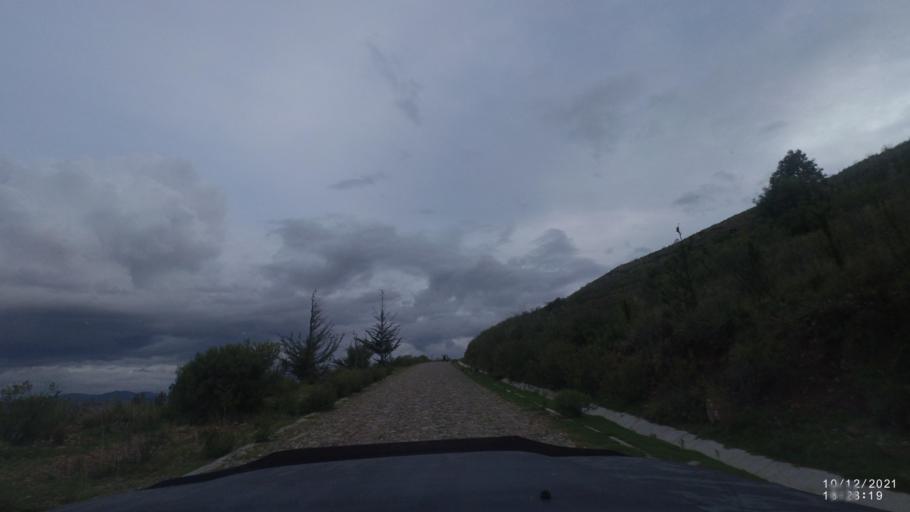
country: BO
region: Cochabamba
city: Tarata
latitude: -17.8070
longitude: -65.9766
